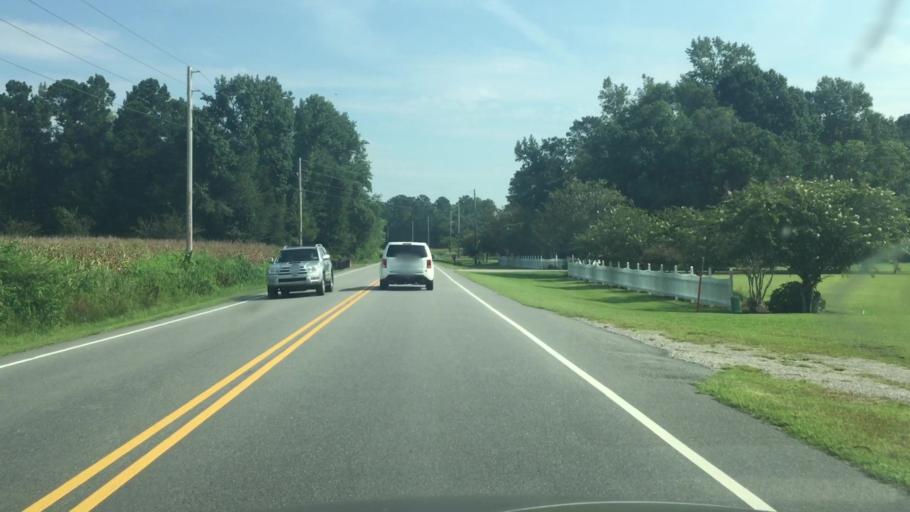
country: US
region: North Carolina
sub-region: Columbus County
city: Tabor City
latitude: 34.2134
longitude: -78.8247
